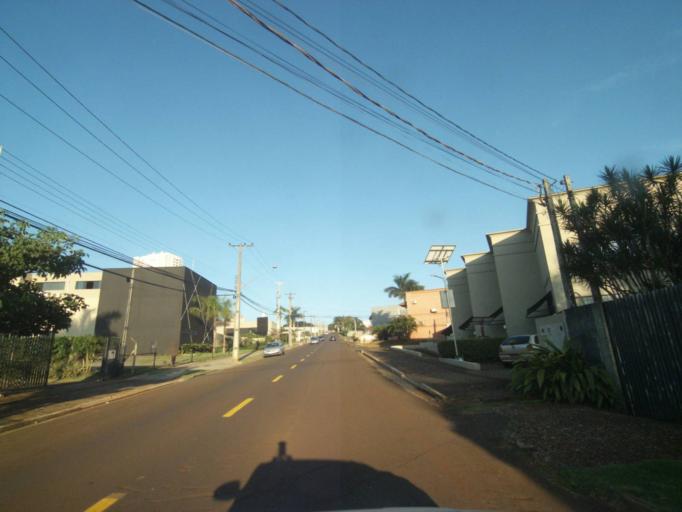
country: BR
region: Parana
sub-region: Londrina
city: Londrina
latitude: -23.3458
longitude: -51.1930
